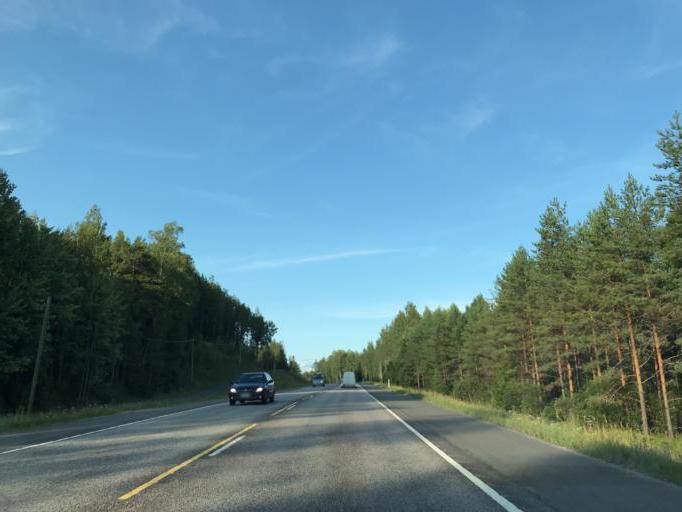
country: FI
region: Uusimaa
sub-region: Helsinki
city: Vihti
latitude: 60.3910
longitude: 24.3225
